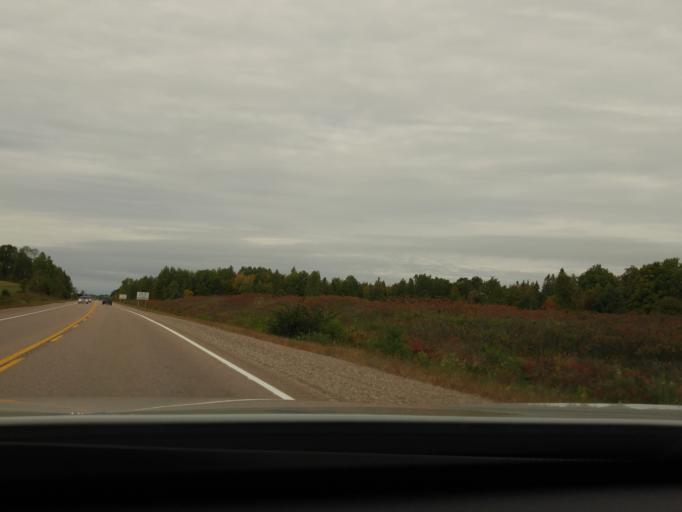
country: CA
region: Ontario
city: Renfrew
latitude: 45.5653
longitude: -76.7571
